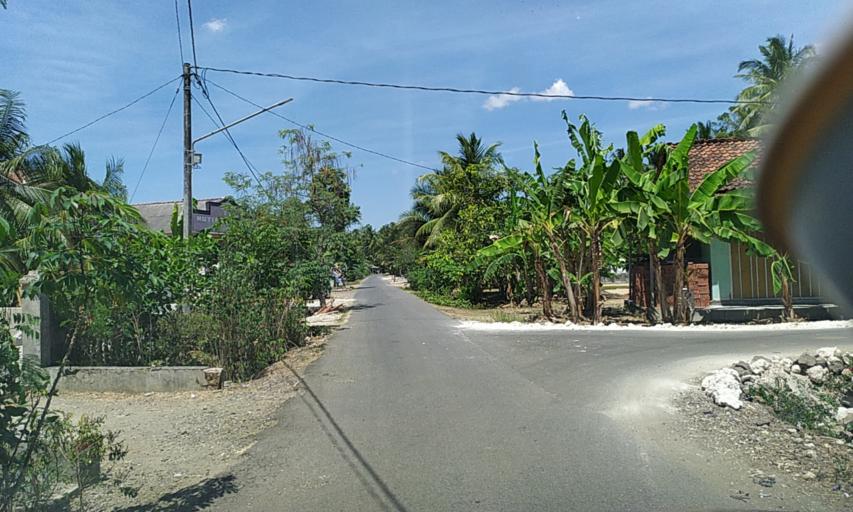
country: ID
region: Central Java
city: Kalenaren
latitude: -7.5830
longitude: 108.7756
